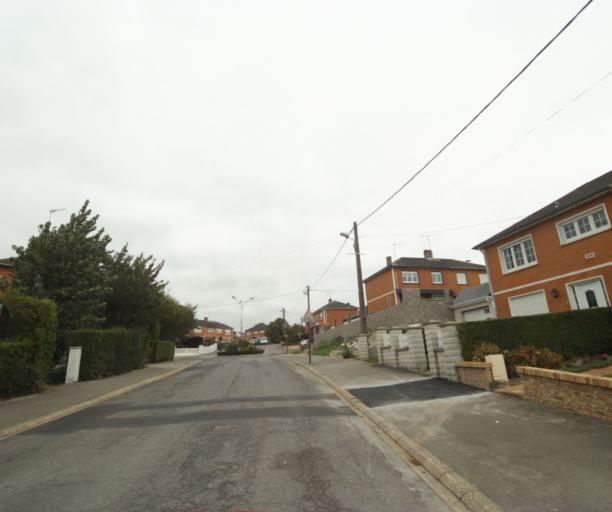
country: FR
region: Nord-Pas-de-Calais
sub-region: Departement du Pas-de-Calais
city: Etaples
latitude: 50.5222
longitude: 1.6351
